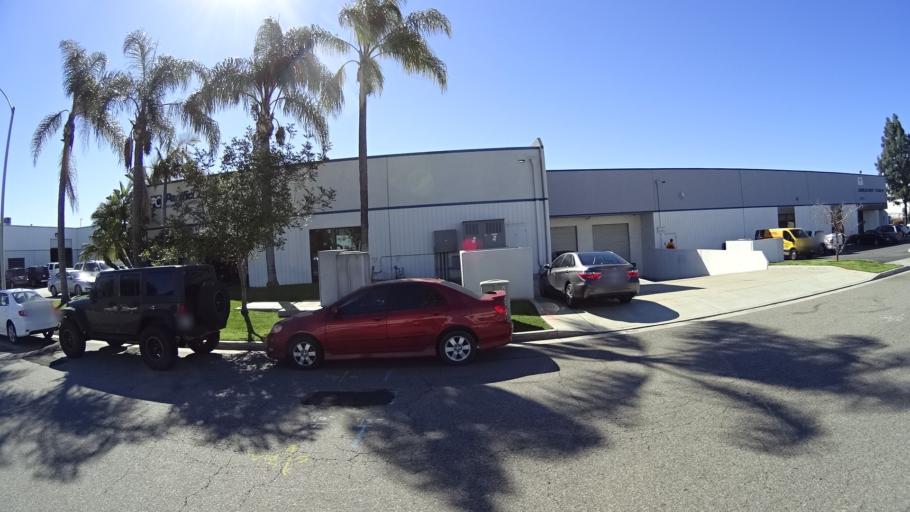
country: US
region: California
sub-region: Orange County
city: Yorba Linda
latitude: 33.8628
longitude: -117.8014
